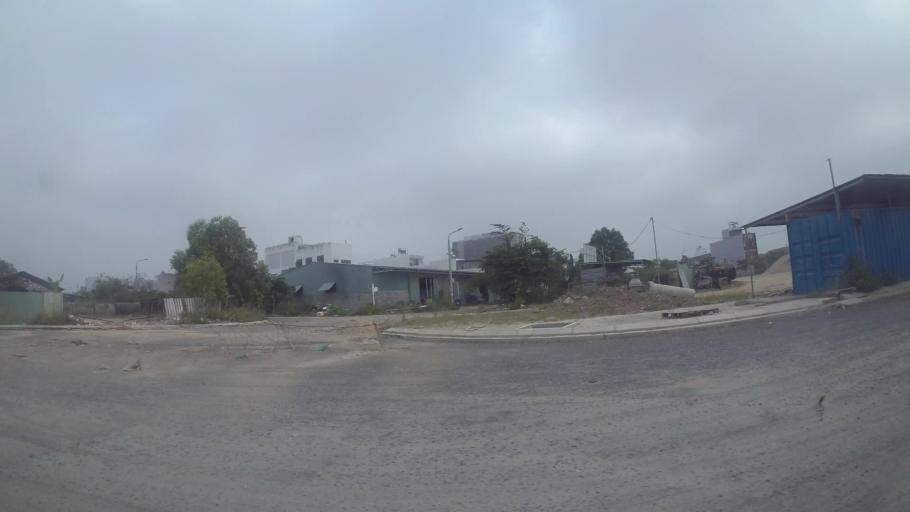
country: VN
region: Da Nang
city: Ngu Hanh Son
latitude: 16.0193
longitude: 108.2461
